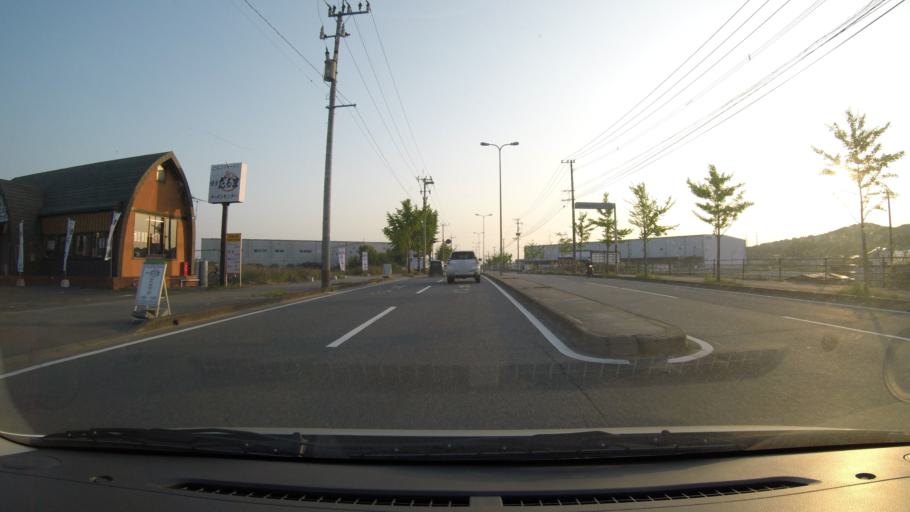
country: JP
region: Fukuoka
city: Sasaguri
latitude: 33.6382
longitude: 130.4891
